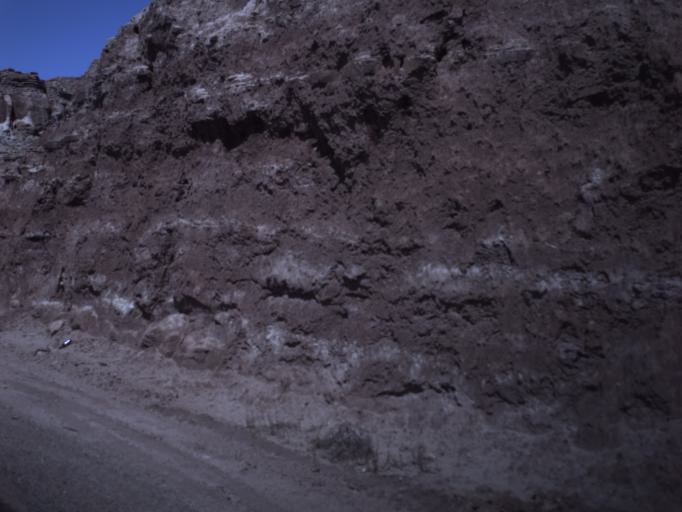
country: US
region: Utah
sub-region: San Juan County
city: Blanding
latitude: 37.2582
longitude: -109.2660
